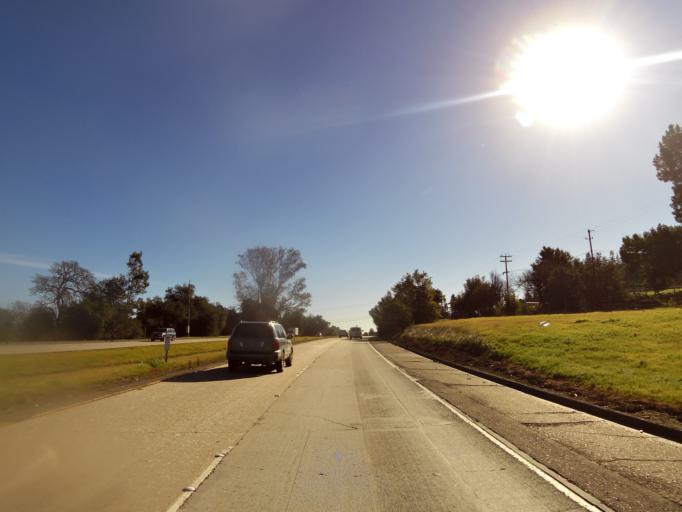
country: US
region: California
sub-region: Sonoma County
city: Cloverdale
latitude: 38.7745
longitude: -123.0010
